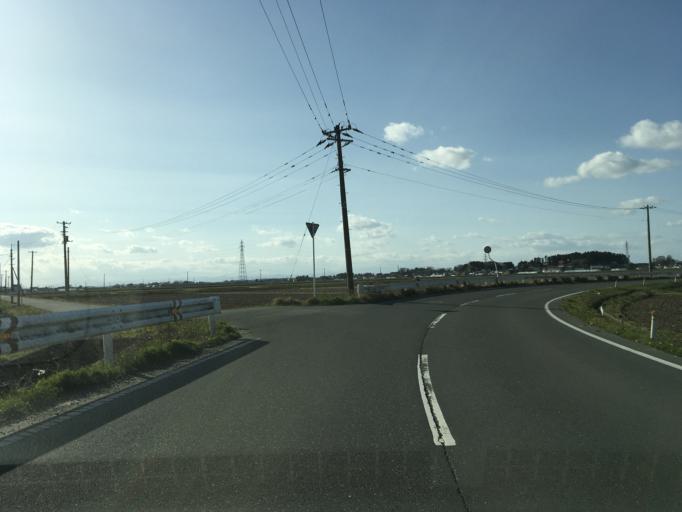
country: JP
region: Miyagi
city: Wakuya
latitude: 38.6592
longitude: 141.2302
